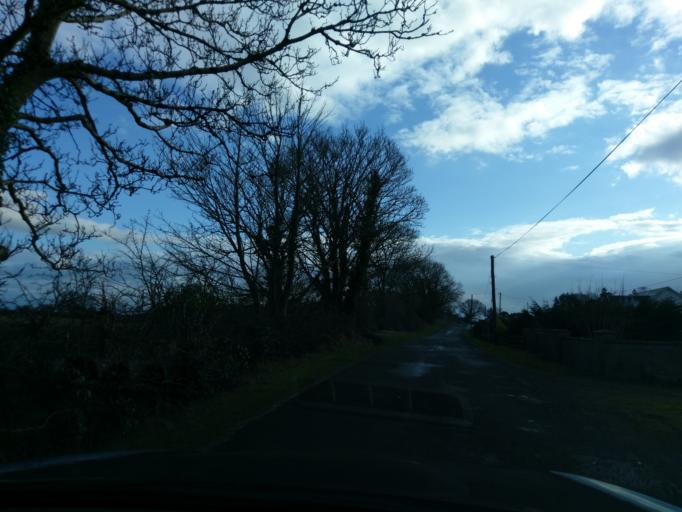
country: IE
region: Connaught
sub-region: County Galway
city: Athenry
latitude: 53.3903
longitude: -8.6229
